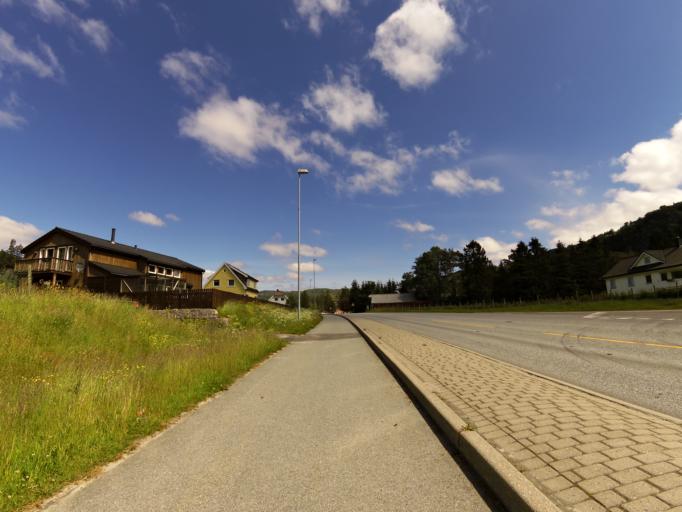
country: NO
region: Vest-Agder
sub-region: Kvinesdal
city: Liknes
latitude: 58.3066
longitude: 6.9552
